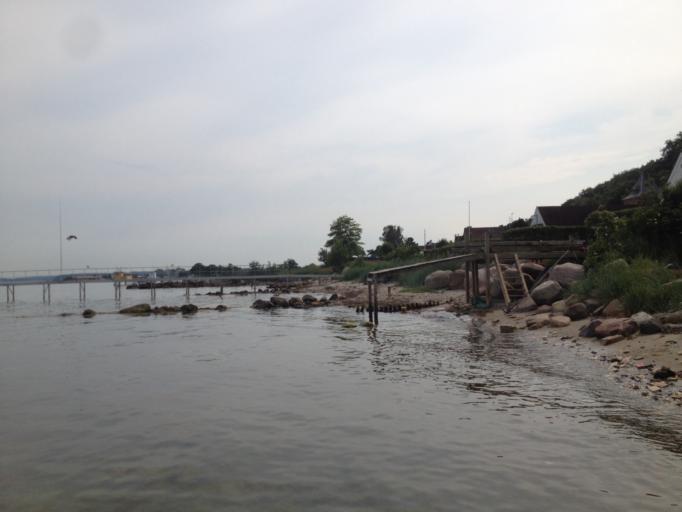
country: DK
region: Capital Region
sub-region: Fredensborg Kommune
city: Humlebaek
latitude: 55.9470
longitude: 12.5301
